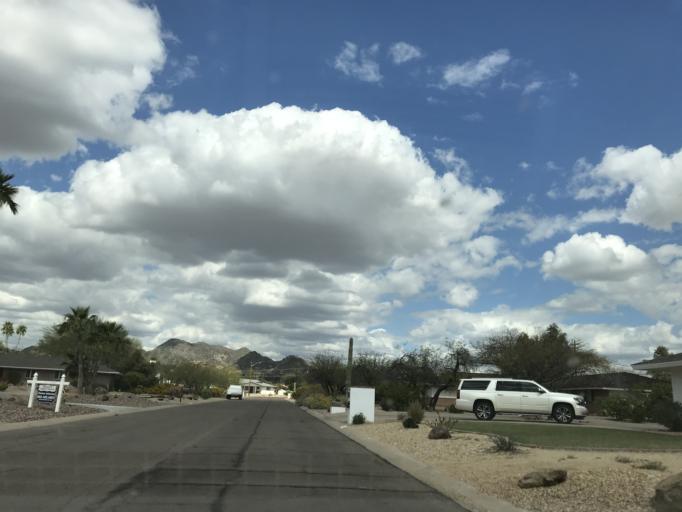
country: US
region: Arizona
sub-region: Maricopa County
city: Paradise Valley
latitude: 33.5143
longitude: -111.9904
